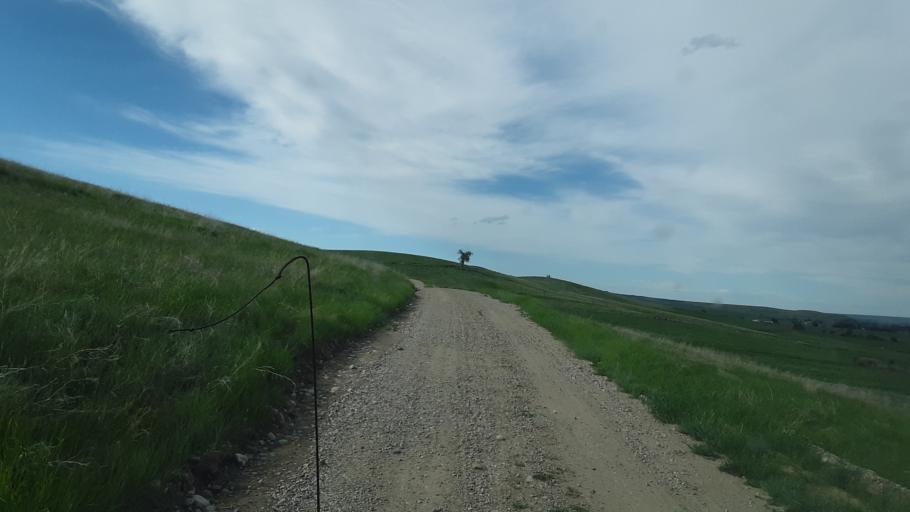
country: US
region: Montana
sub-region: Carbon County
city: Red Lodge
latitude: 45.3677
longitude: -109.1901
